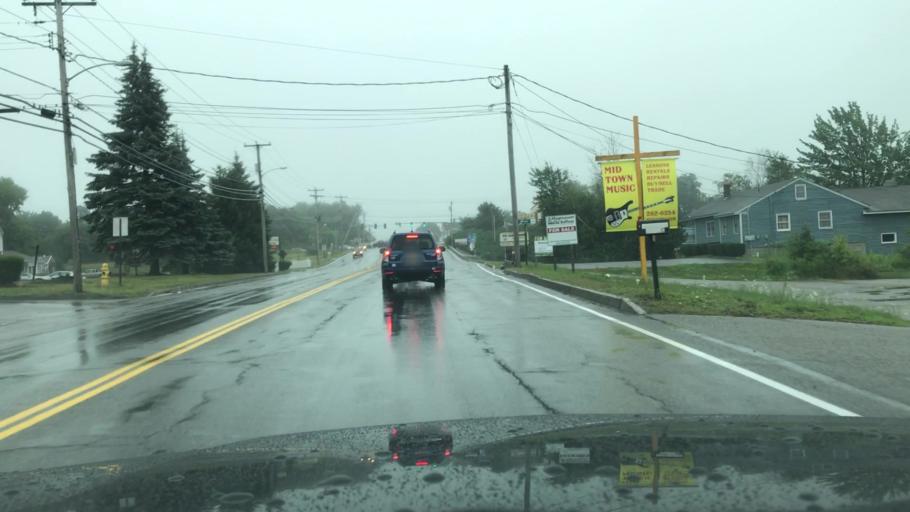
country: US
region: Maine
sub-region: York County
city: Biddeford
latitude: 43.4676
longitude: -70.4865
